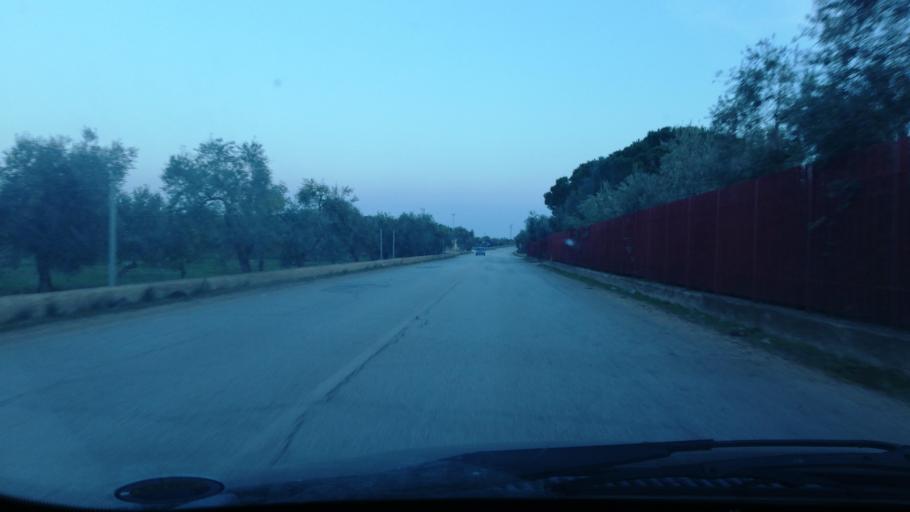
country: IT
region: Apulia
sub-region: Provincia di Bari
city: Bitonto
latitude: 41.1296
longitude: 16.7100
